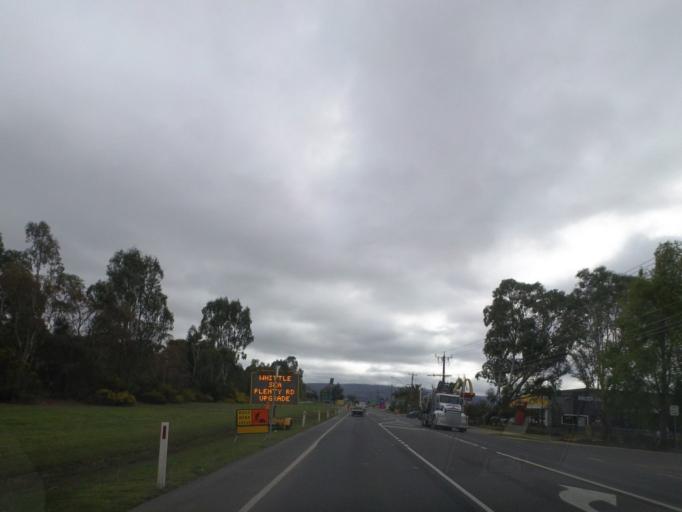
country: AU
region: Victoria
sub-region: Whittlesea
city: Whittlesea
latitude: -37.5171
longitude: 145.1141
